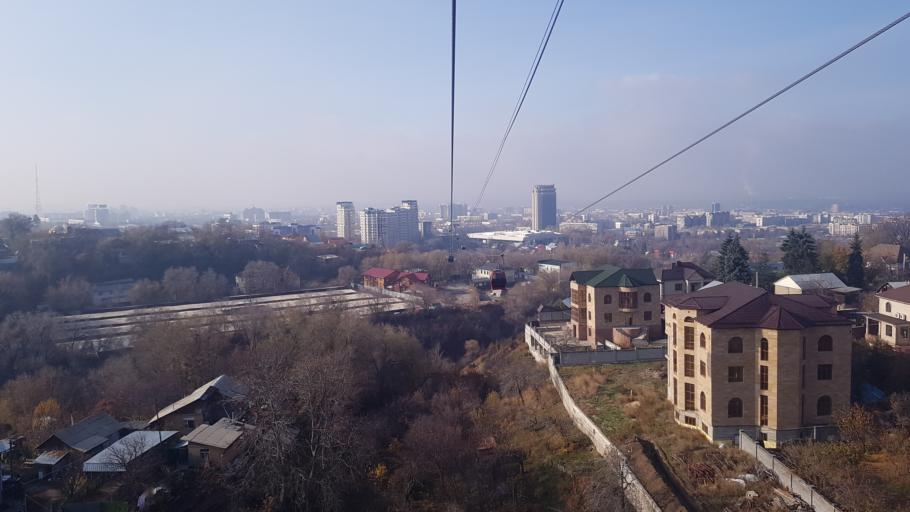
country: KZ
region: Almaty Qalasy
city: Almaty
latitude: 43.2371
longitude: 76.9697
